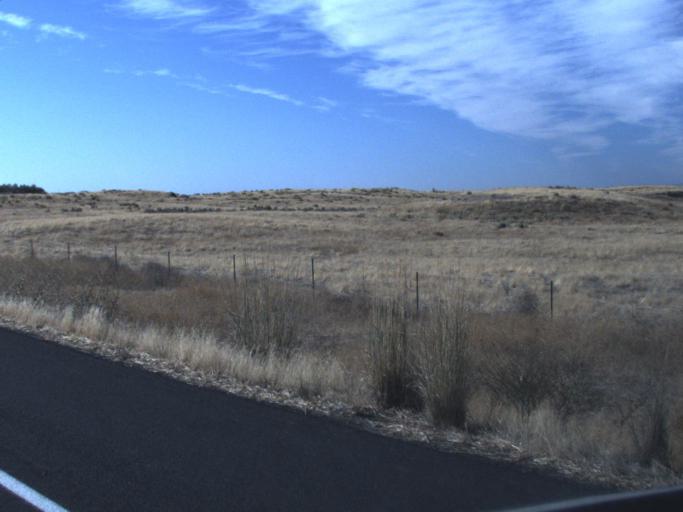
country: US
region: Washington
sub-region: Franklin County
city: Connell
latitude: 46.6390
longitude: -119.0064
